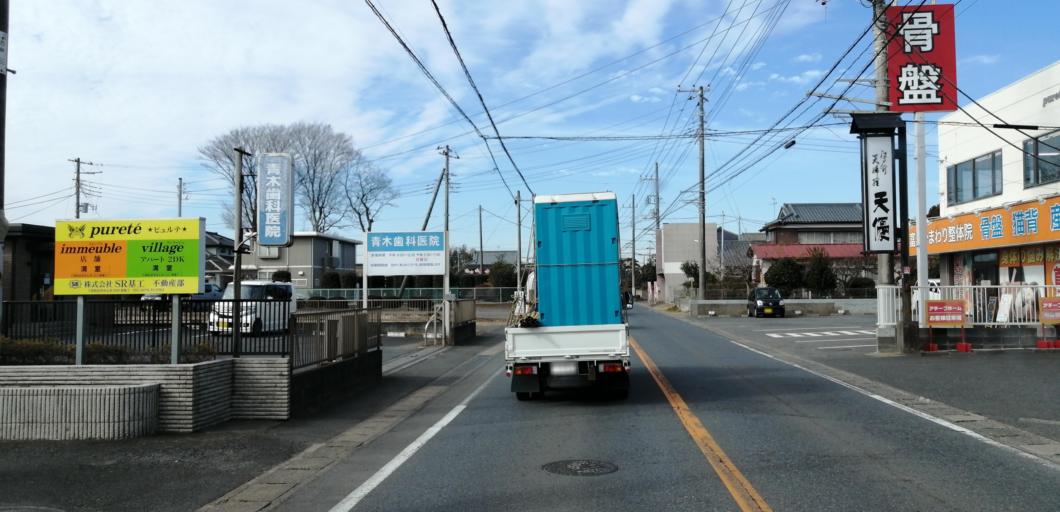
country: JP
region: Chiba
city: Narita
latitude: 35.7369
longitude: 140.3233
